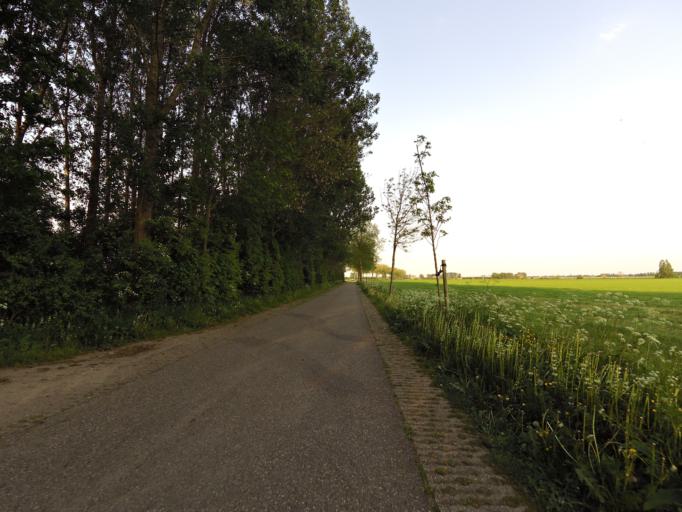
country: NL
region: Gelderland
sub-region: Oude IJsselstreek
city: Gendringen
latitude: 51.8538
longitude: 6.3295
